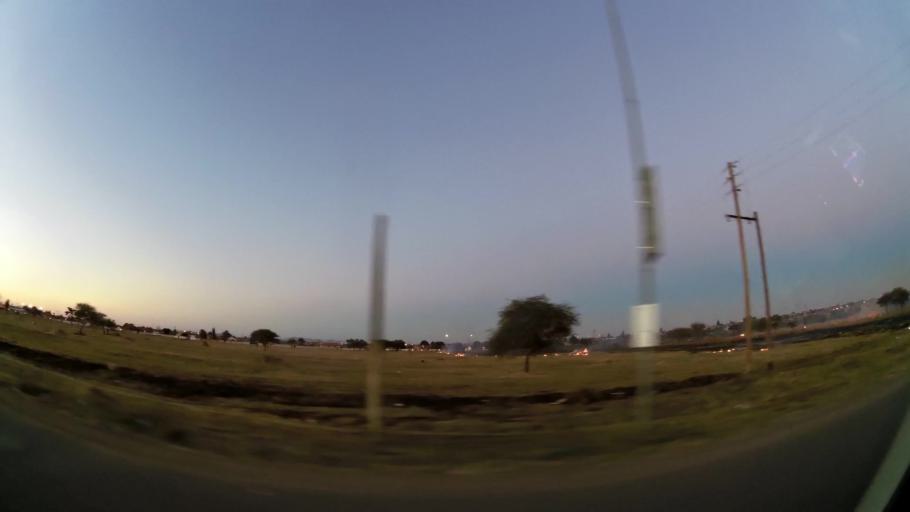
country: ZA
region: Limpopo
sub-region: Capricorn District Municipality
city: Polokwane
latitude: -23.8556
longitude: 29.4011
